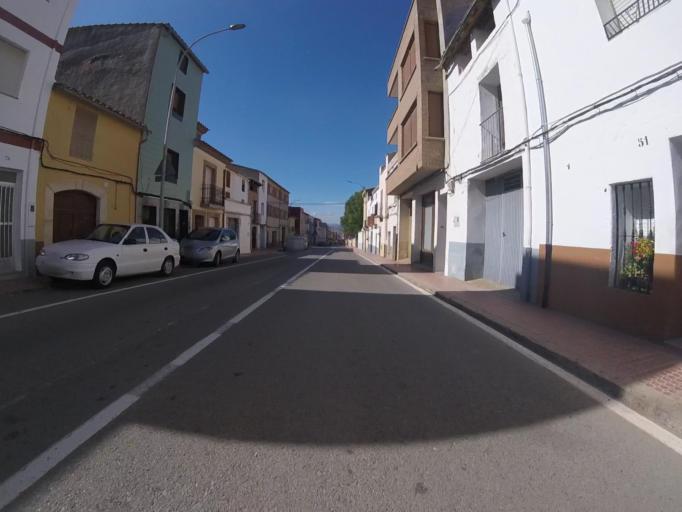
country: ES
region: Valencia
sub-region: Provincia de Castello
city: Albocasser
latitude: 40.3574
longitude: 0.0288
